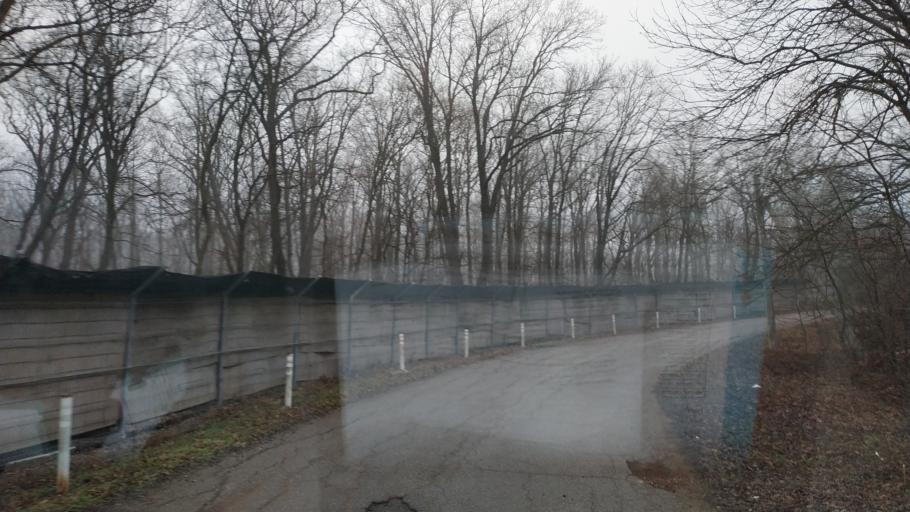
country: MD
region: Laloveni
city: Ialoveni
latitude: 46.9501
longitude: 28.7005
